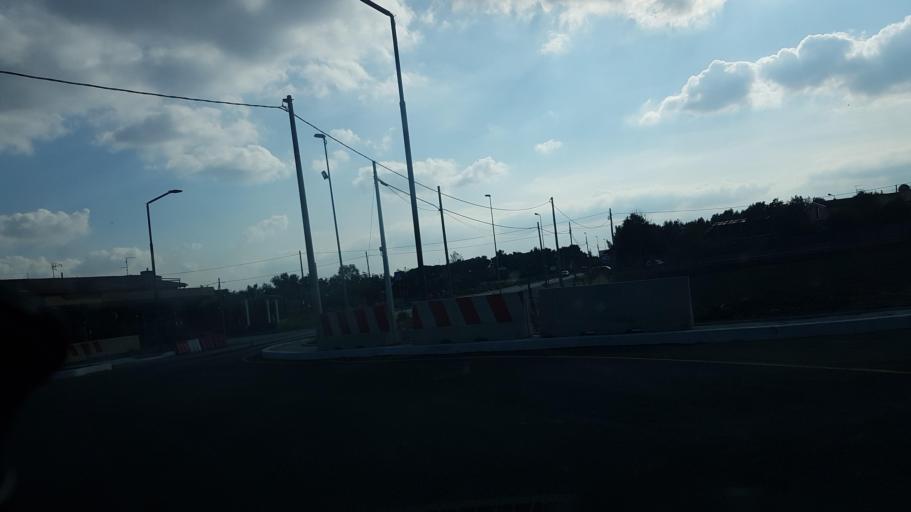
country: IT
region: Apulia
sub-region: Provincia di Foggia
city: Foggia
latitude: 41.4456
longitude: 15.5267
